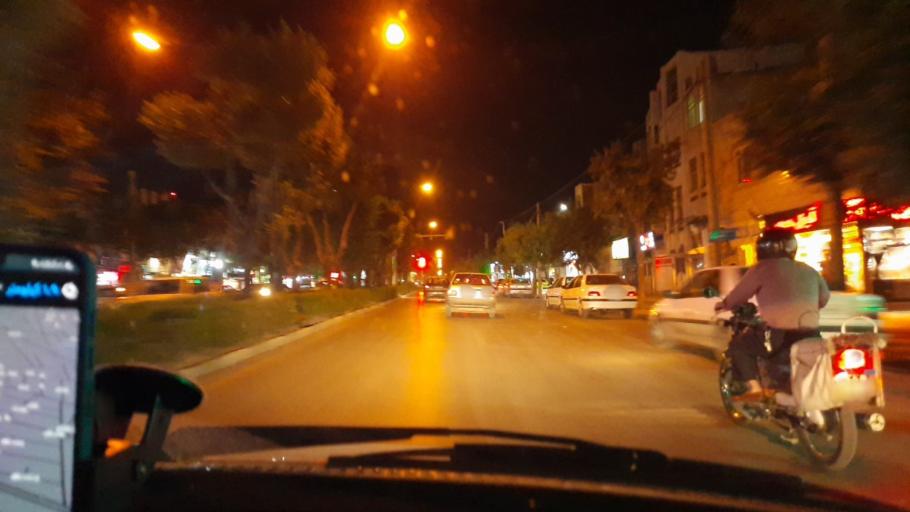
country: IR
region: Markazi
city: Arak
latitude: 34.1044
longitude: 49.6953
